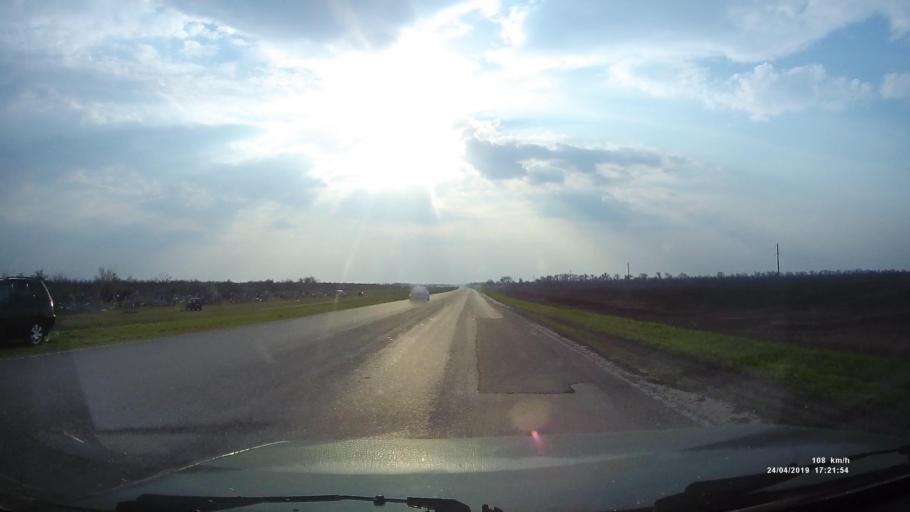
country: RU
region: Rostov
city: Gigant
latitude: 46.5204
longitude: 41.3216
